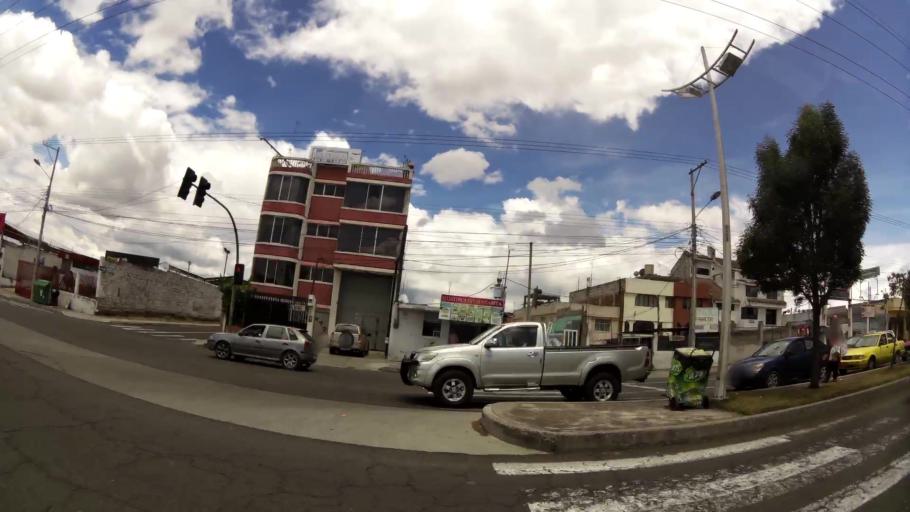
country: EC
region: Tungurahua
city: Ambato
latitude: -1.2602
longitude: -78.6134
